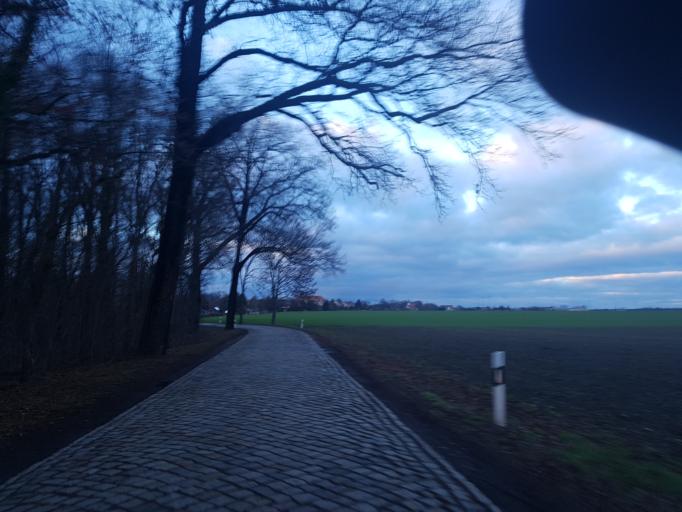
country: DE
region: Brandenburg
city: Muhlberg
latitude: 51.4664
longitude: 13.2056
